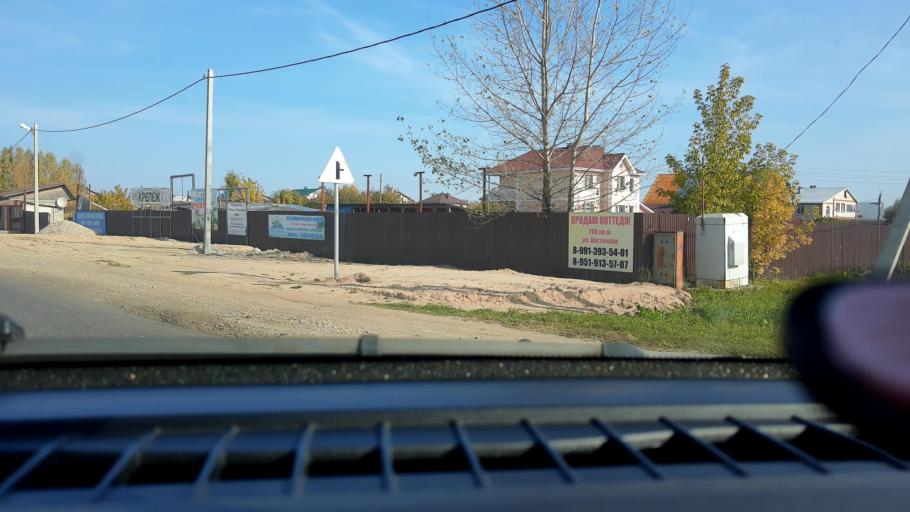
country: RU
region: Nizjnij Novgorod
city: Kstovo
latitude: 56.1474
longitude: 44.2308
